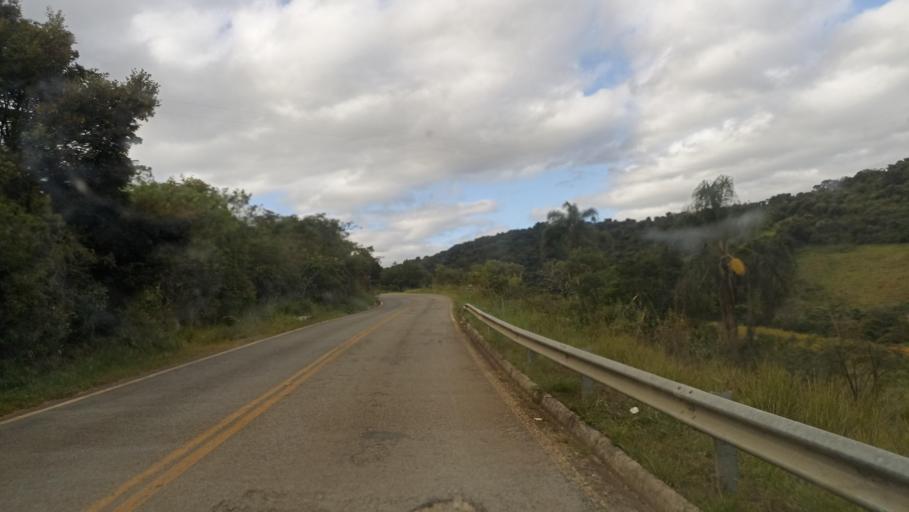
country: BR
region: Minas Gerais
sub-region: Tiradentes
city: Tiradentes
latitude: -21.0776
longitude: -44.0744
